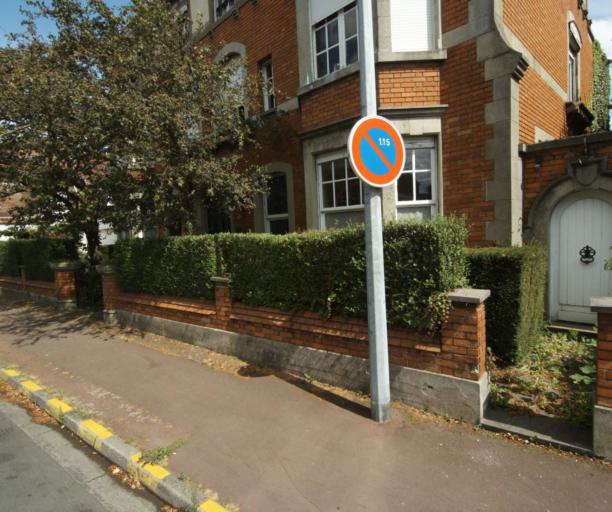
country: FR
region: Nord-Pas-de-Calais
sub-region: Departement du Nord
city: Mouvaux
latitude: 50.6972
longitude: 3.1461
